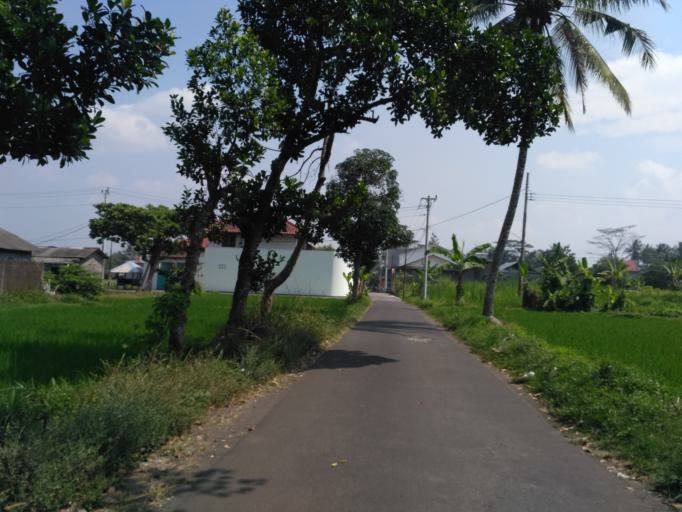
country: ID
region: Daerah Istimewa Yogyakarta
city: Melati
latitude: -7.7077
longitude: 110.4125
